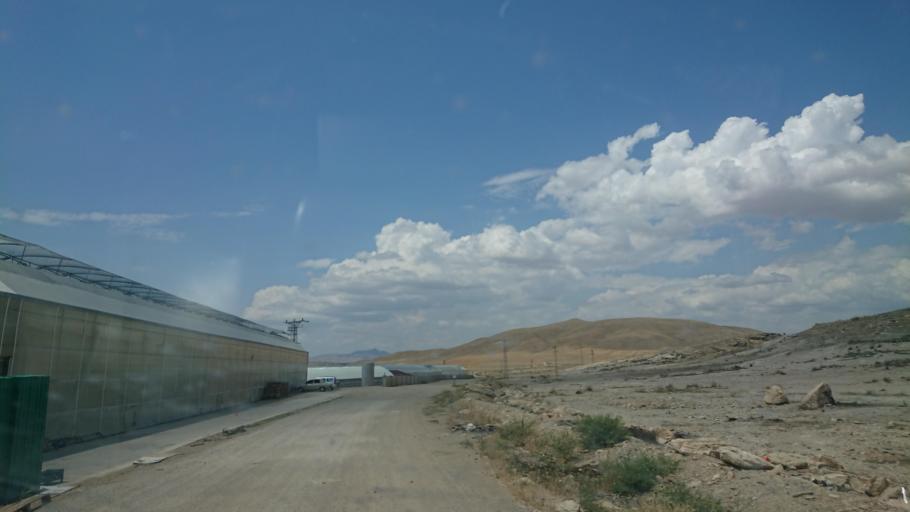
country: TR
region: Aksaray
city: Sariyahsi
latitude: 38.9986
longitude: 33.9126
